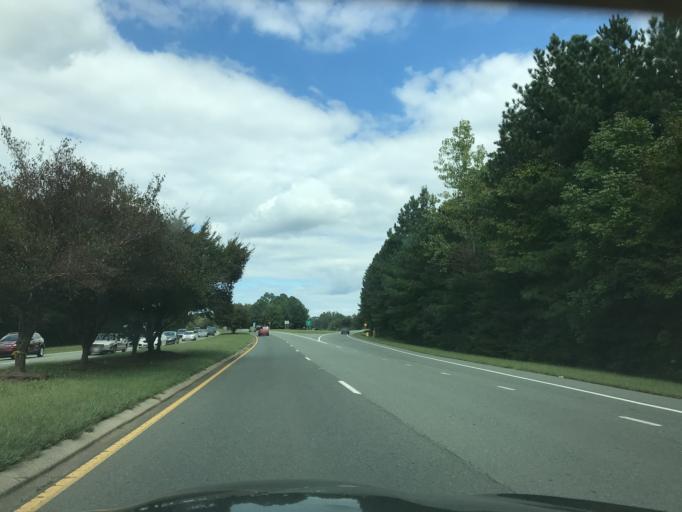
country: US
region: North Carolina
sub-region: Orange County
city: Chapel Hill
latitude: 35.9056
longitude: -79.0292
